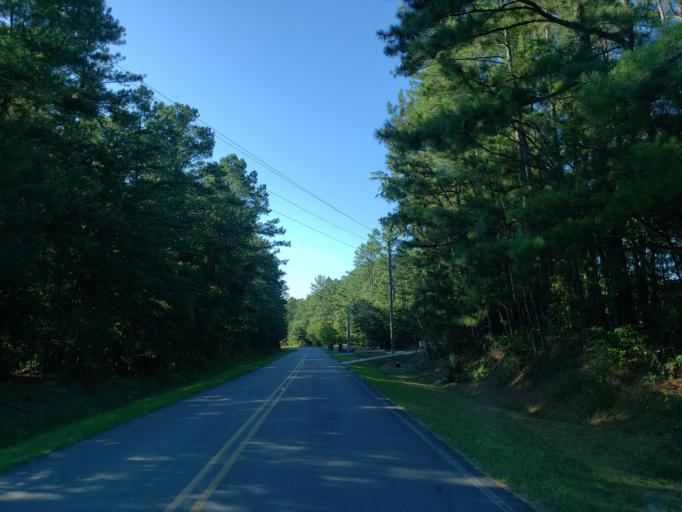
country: US
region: Georgia
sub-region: Bartow County
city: Euharlee
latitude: 34.1164
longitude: -85.0106
